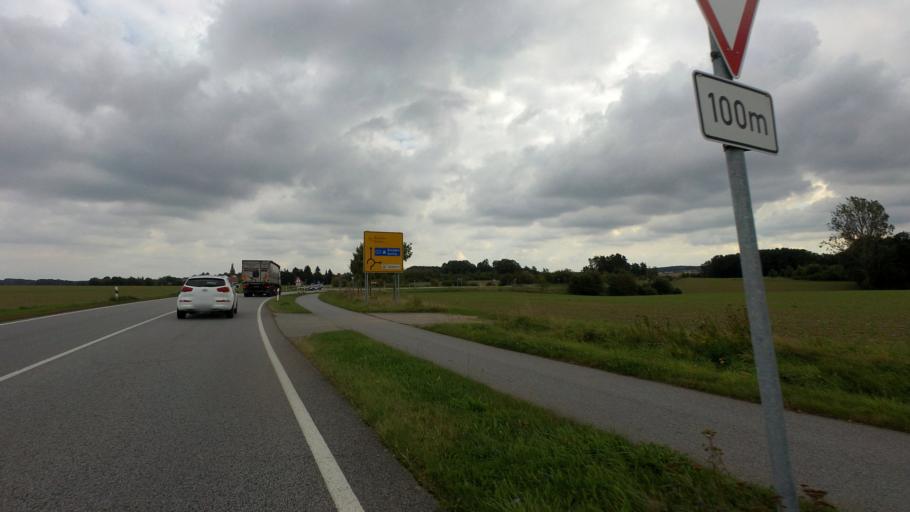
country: DE
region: Saxony
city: Radibor
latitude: 51.2300
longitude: 14.3785
